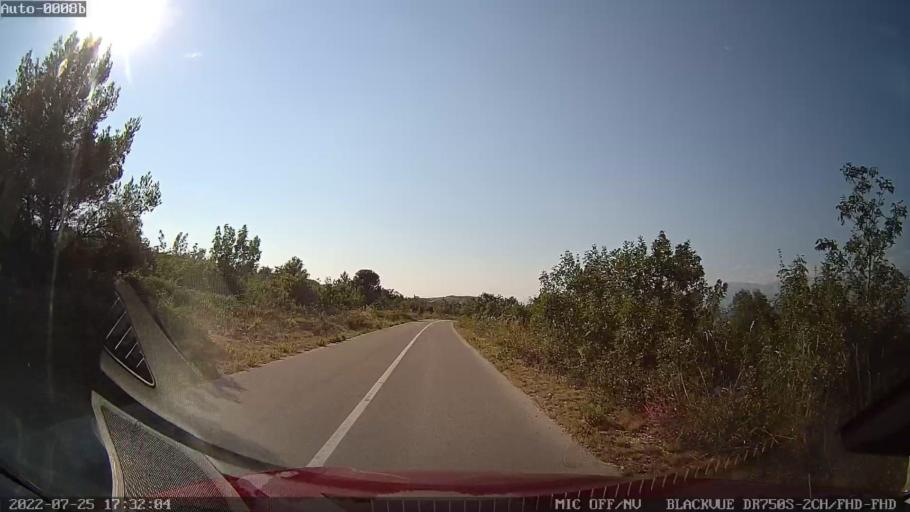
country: HR
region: Zadarska
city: Posedarje
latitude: 44.1740
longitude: 15.4958
